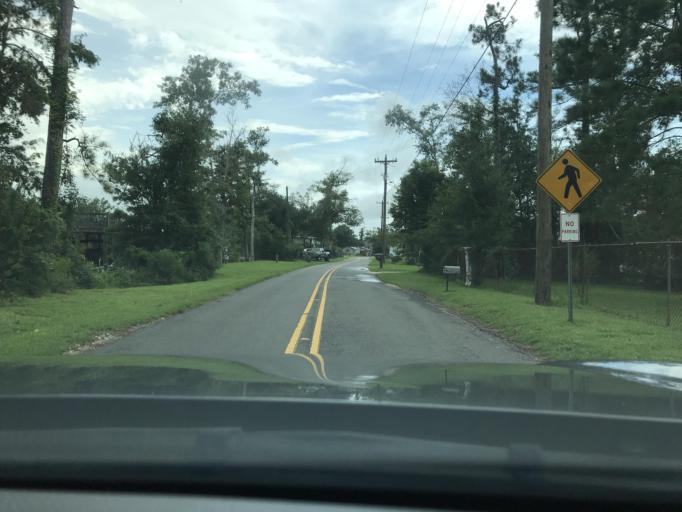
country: US
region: Louisiana
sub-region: Calcasieu Parish
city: Moss Bluff
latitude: 30.2837
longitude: -93.2299
